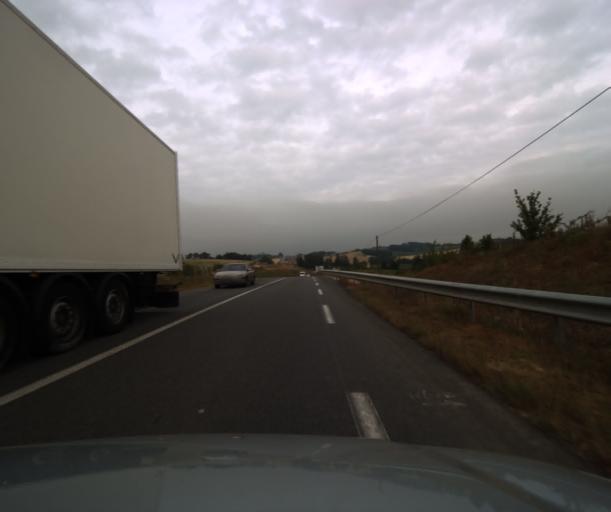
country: FR
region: Midi-Pyrenees
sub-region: Departement du Gers
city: Aubiet
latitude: 43.6476
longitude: 0.7283
